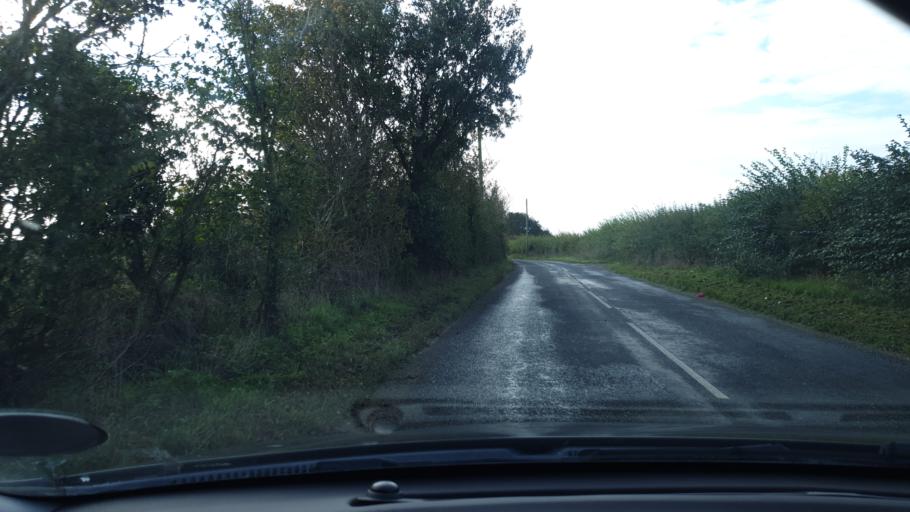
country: GB
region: England
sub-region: Essex
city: Manningtree
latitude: 51.9330
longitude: 1.0480
